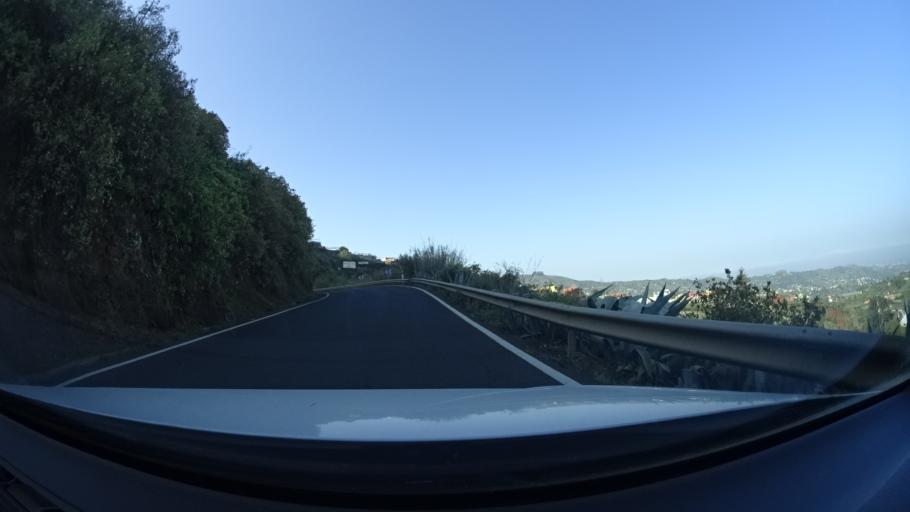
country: ES
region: Canary Islands
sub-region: Provincia de Las Palmas
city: Vega de San Mateo
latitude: 28.0115
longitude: -15.5354
